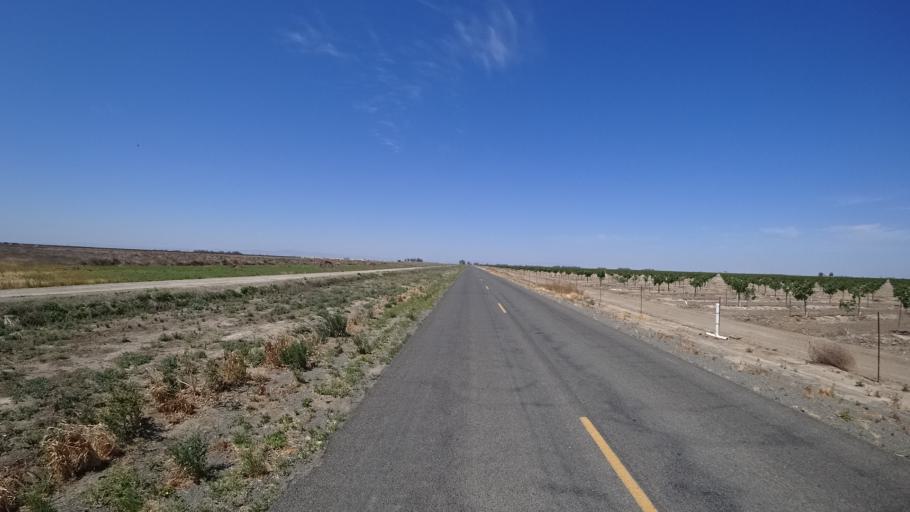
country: US
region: California
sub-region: Kings County
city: Stratford
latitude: 36.1892
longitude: -119.7327
